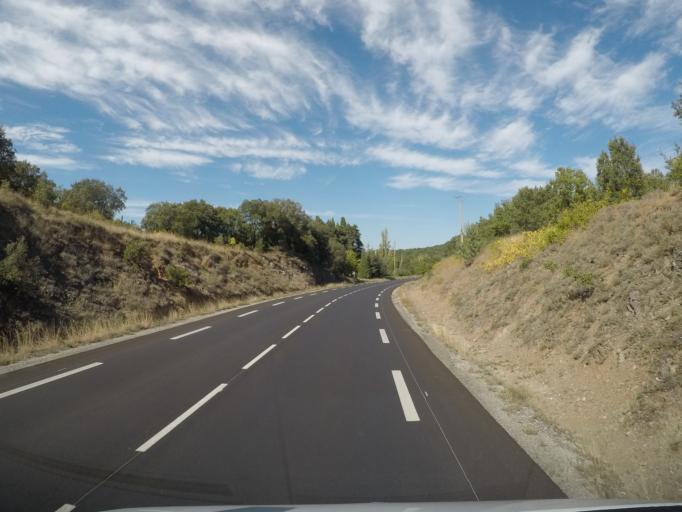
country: FR
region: Languedoc-Roussillon
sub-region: Departement du Gard
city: Sauve
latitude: 43.9750
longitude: 3.9247
